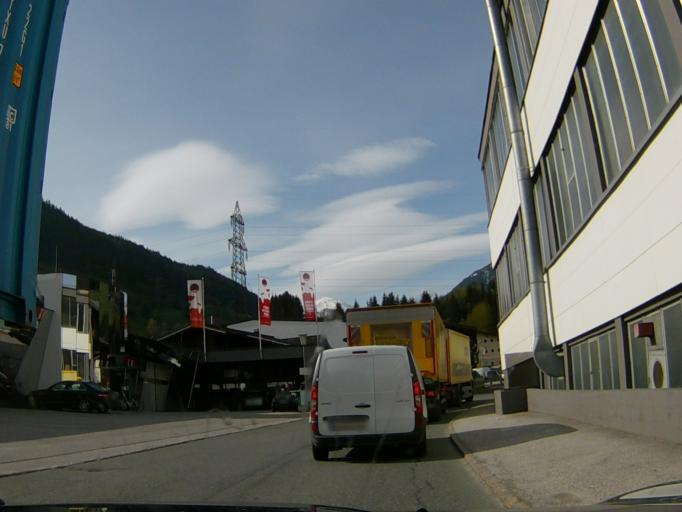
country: AT
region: Salzburg
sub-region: Politischer Bezirk Zell am See
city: Mittersill
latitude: 47.2772
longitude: 12.4845
